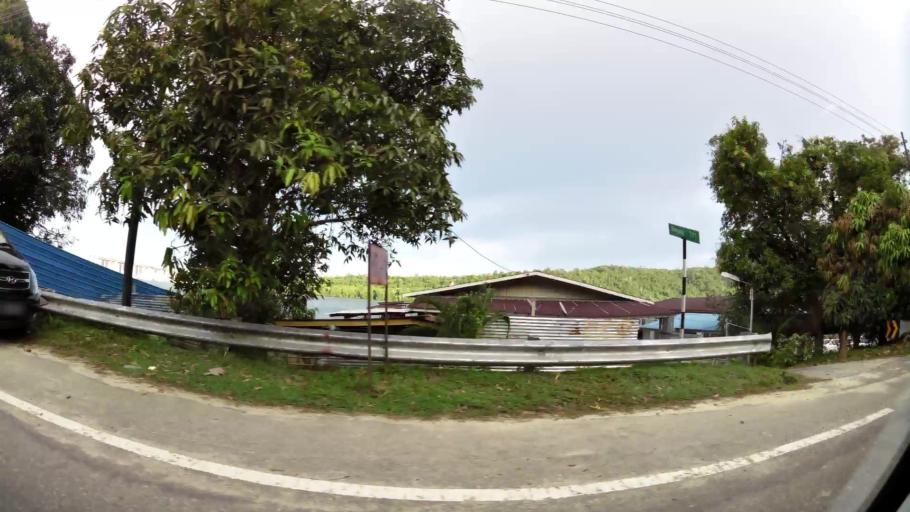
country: BN
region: Brunei and Muara
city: Bandar Seri Begawan
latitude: 4.9233
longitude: 115.0114
